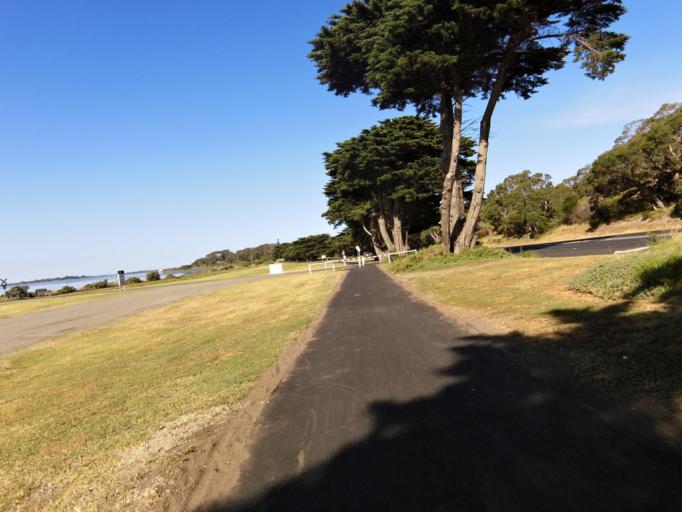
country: AU
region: Victoria
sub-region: Queenscliffe
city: Queenscliff
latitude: -38.2708
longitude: 144.6393
